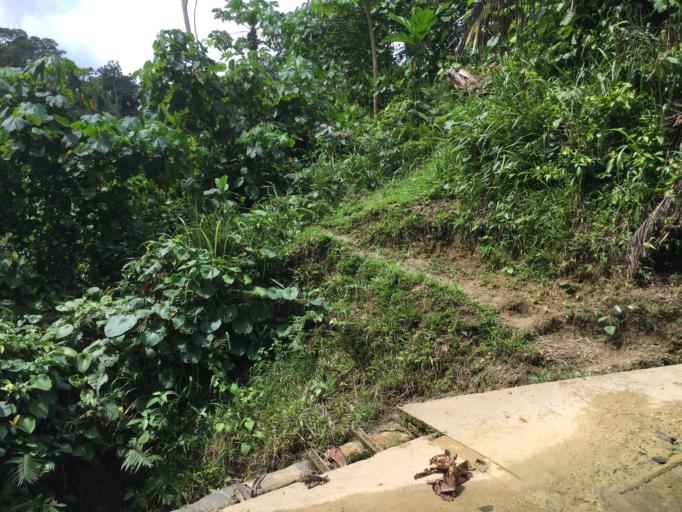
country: PG
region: Gulf
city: Kerema
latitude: -7.9850
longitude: 145.8295
